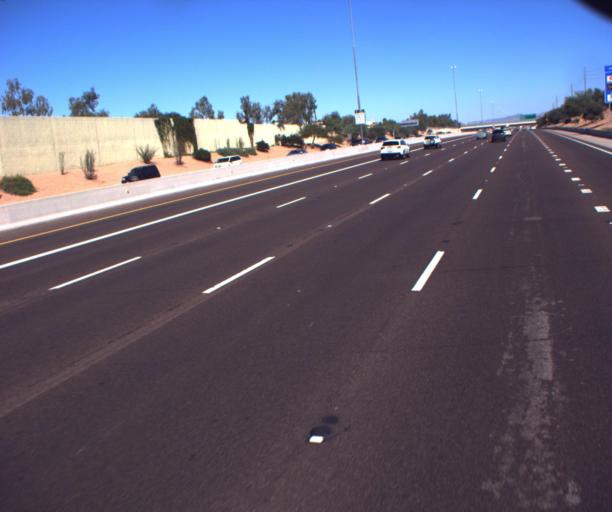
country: US
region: Arizona
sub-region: Maricopa County
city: Paradise Valley
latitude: 33.6061
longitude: -111.8913
